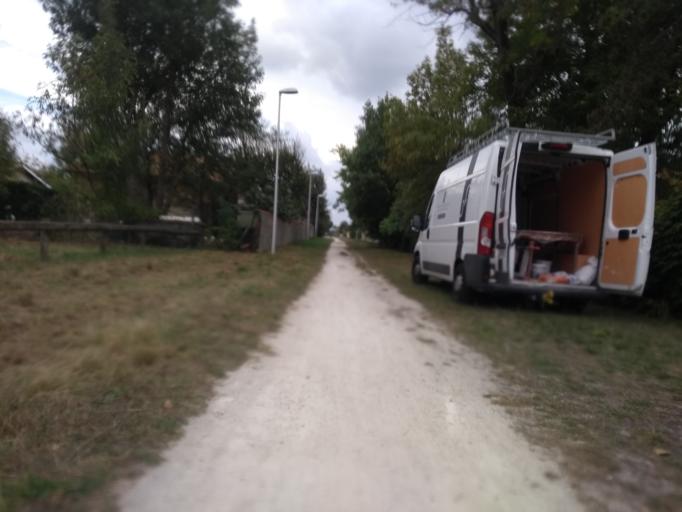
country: FR
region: Aquitaine
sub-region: Departement de la Gironde
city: Pessac
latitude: 44.8096
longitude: -0.6554
